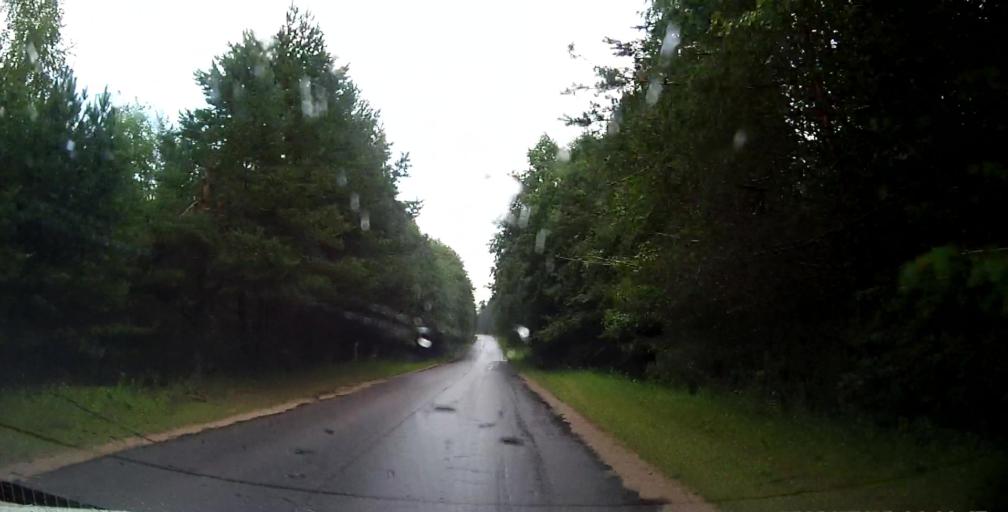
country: RU
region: Smolensk
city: Demidov
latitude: 55.4589
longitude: 31.6091
